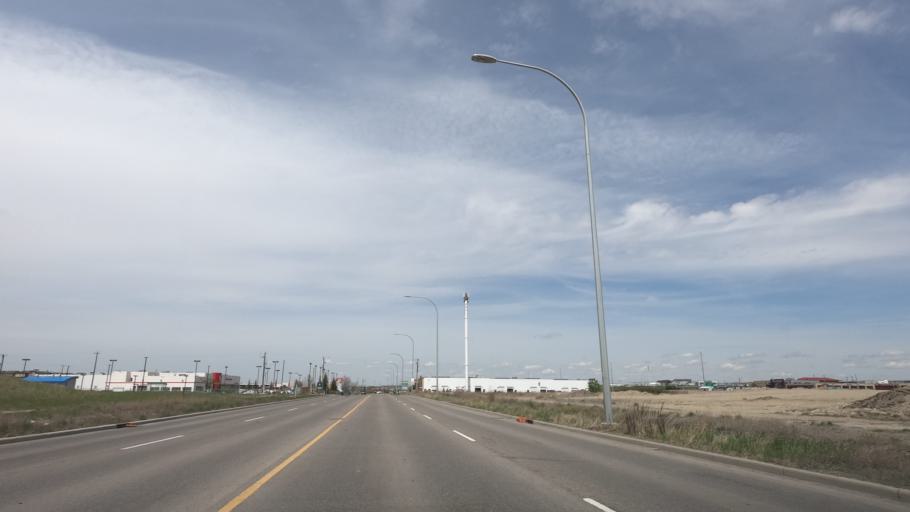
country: CA
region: Alberta
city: Airdrie
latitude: 51.2562
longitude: -114.0051
